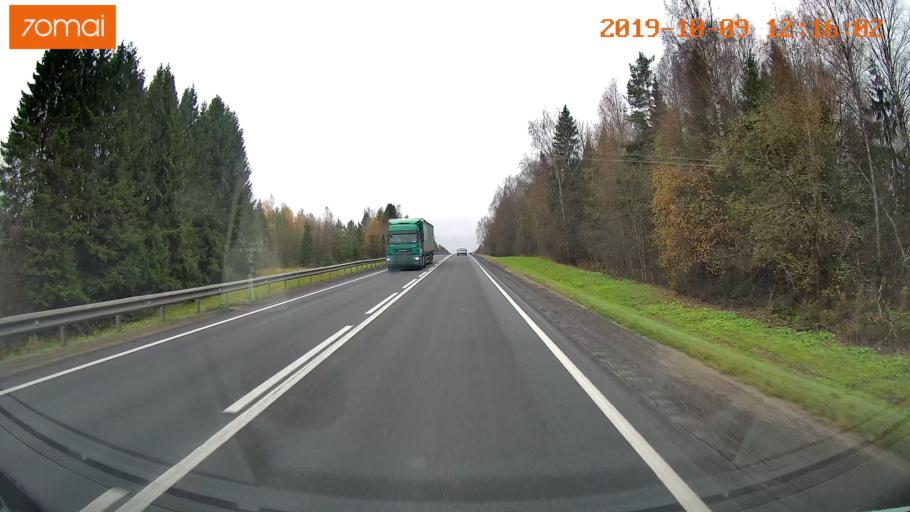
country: RU
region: Jaroslavl
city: Prechistoye
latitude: 58.4744
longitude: 40.3218
